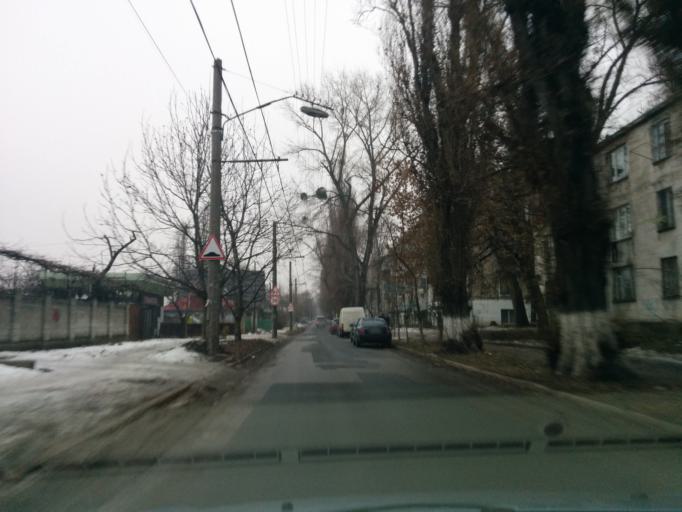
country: MD
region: Chisinau
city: Chisinau
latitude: 46.9997
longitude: 28.8621
